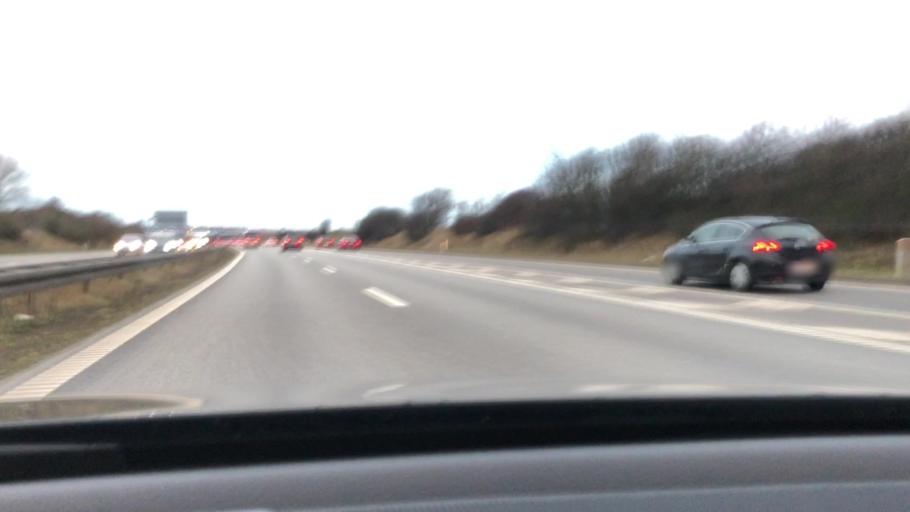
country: DK
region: Central Jutland
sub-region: Randers Kommune
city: Randers
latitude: 56.4156
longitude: 10.0750
